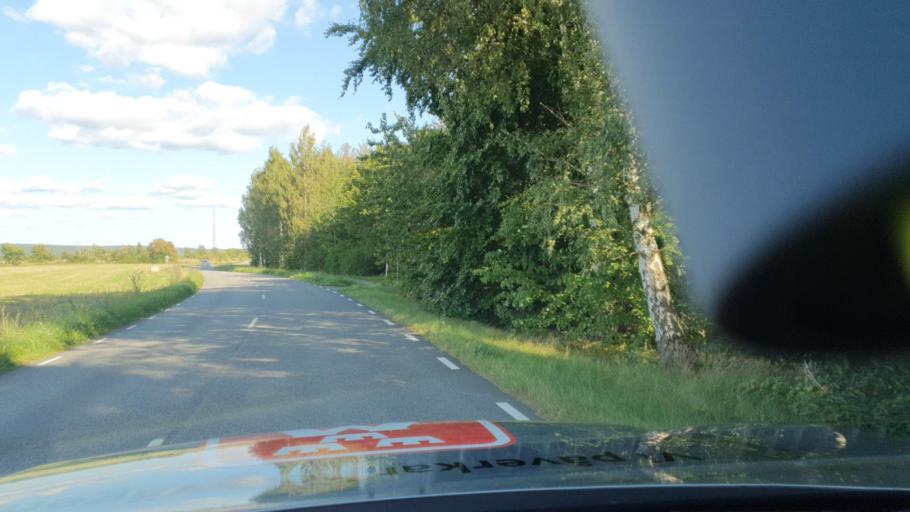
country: SE
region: Skane
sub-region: Bromolla Kommun
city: Bromoella
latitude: 56.0857
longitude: 14.4868
